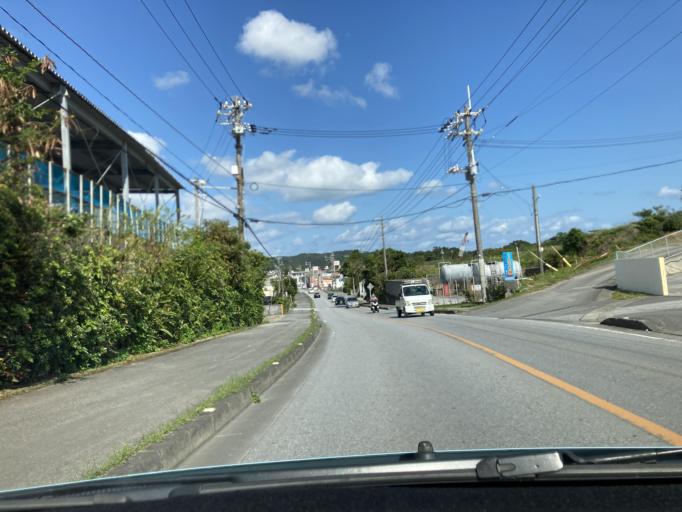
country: JP
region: Okinawa
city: Nago
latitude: 26.6139
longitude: 128.0006
